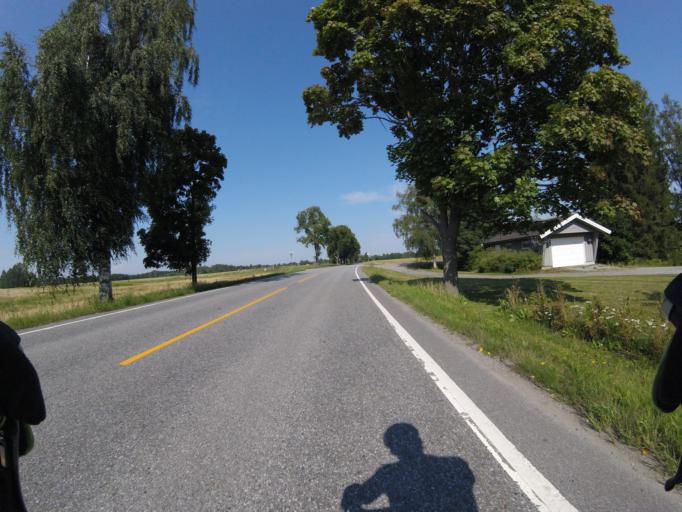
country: NO
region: Akershus
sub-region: Ullensaker
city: Klofta
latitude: 60.0579
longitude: 11.1193
